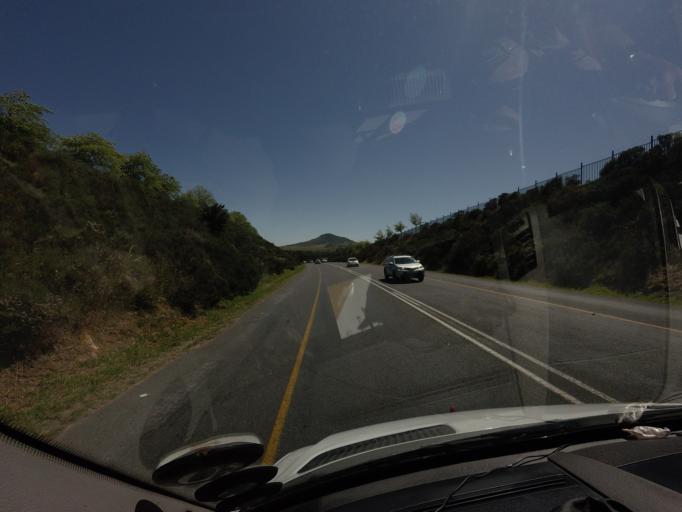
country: ZA
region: Western Cape
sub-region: Cape Winelands District Municipality
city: Stellenbosch
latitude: -33.8772
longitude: 18.8495
